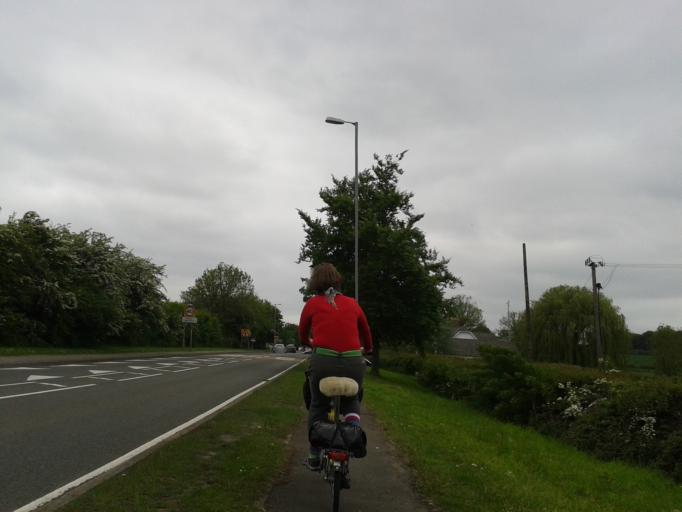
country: GB
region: England
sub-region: Leicestershire
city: Kibworth Harcourt
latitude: 52.5367
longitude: -0.9817
